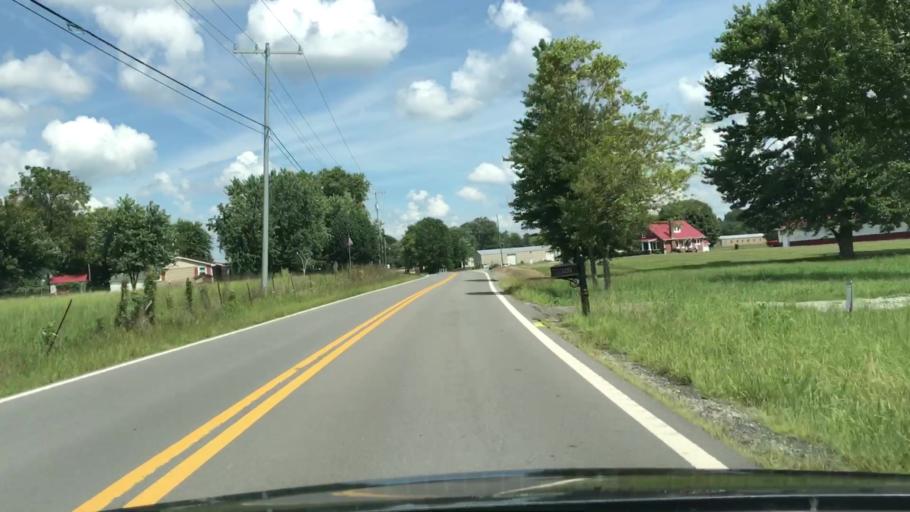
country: US
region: Tennessee
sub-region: Sumner County
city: Portland
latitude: 36.5130
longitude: -86.5722
